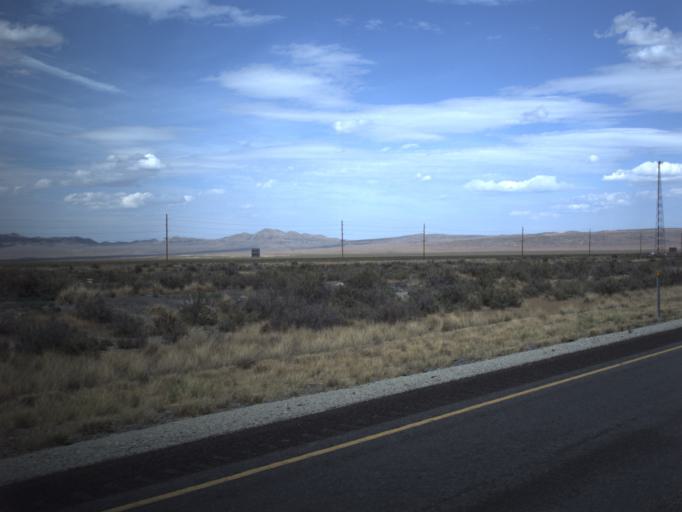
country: US
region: Utah
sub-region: Tooele County
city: Grantsville
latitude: 40.7326
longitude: -113.1096
